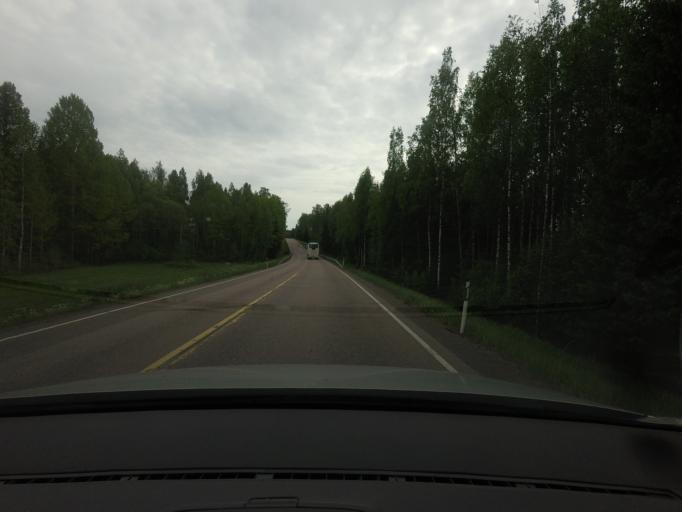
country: FI
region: Kymenlaakso
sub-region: Kotka-Hamina
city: Hamina
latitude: 60.6996
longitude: 27.2885
